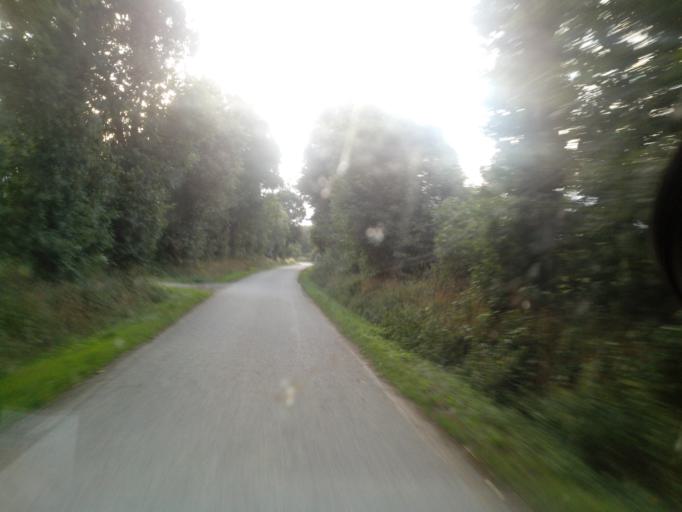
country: FR
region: Brittany
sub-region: Departement du Morbihan
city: Meneac
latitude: 48.1238
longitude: -2.4348
